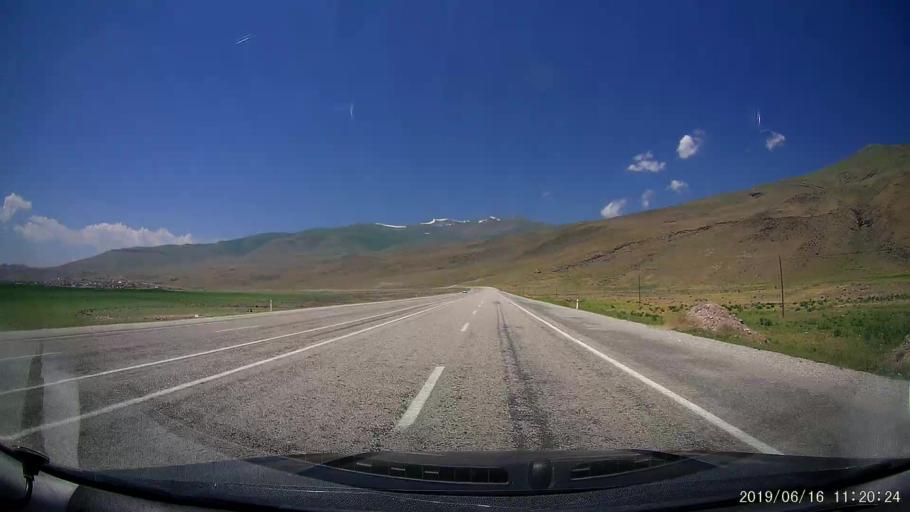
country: TR
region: Agri
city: Dogubayazit
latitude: 39.6987
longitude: 44.0914
